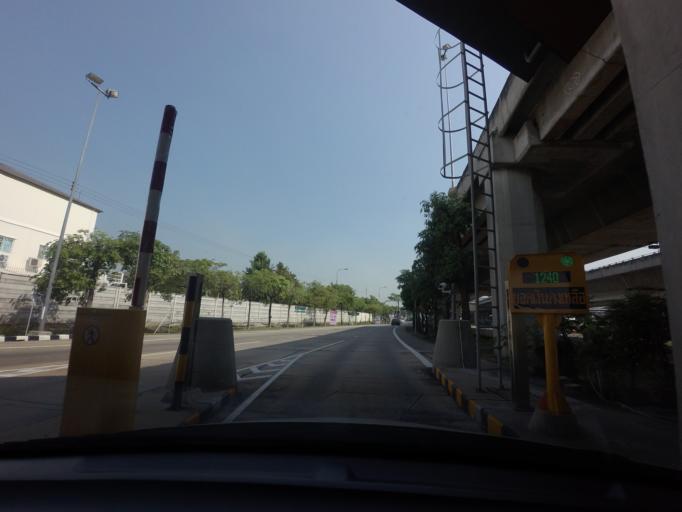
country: TH
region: Bangkok
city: Lak Si
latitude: 13.9158
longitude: 100.5449
